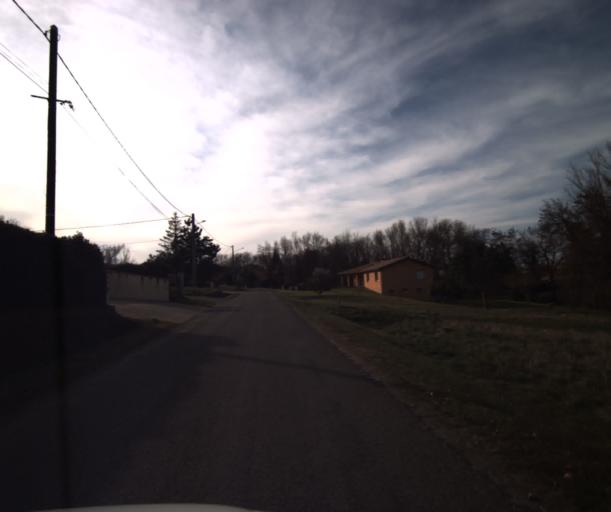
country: FR
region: Midi-Pyrenees
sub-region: Departement du Tarn-et-Garonne
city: Labastide-Saint-Pierre
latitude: 43.9163
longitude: 1.3596
